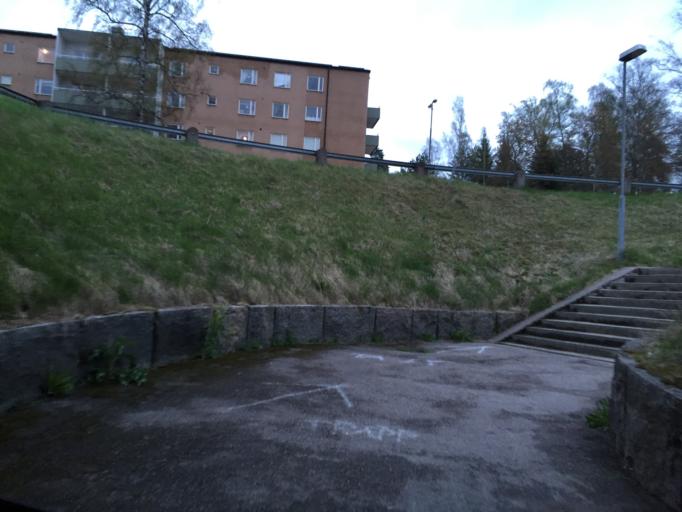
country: SE
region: Dalarna
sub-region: Ludvika Kommun
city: Ludvika
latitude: 60.1409
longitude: 15.1784
